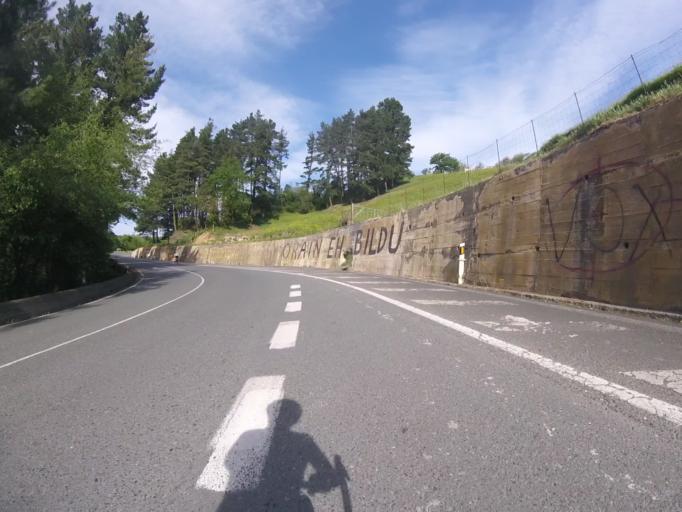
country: ES
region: Basque Country
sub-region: Provincia de Guipuzcoa
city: Zumarraga
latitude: 43.0855
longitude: -2.3050
